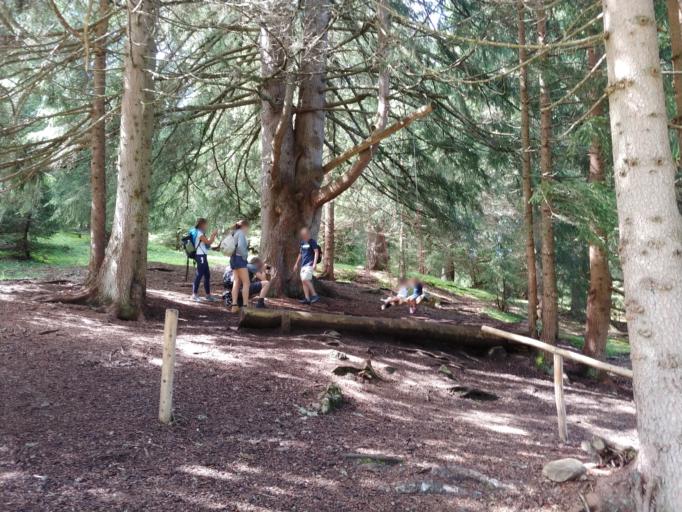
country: IT
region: Trentino-Alto Adige
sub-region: Bolzano
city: Santa Cristina Valgardena
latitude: 46.5467
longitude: 11.7174
